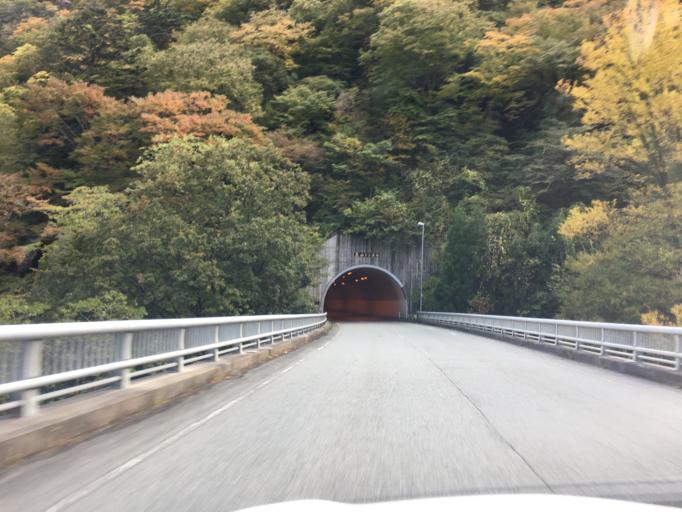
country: JP
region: Fukushima
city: Namie
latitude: 37.3560
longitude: 140.9389
